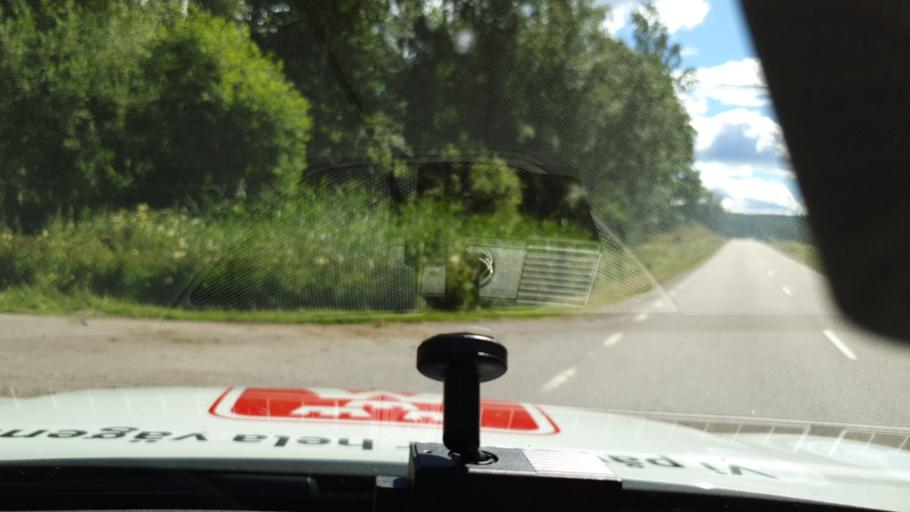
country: SE
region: Vaermland
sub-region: Arvika Kommun
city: Arvika
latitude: 59.6545
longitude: 12.8891
